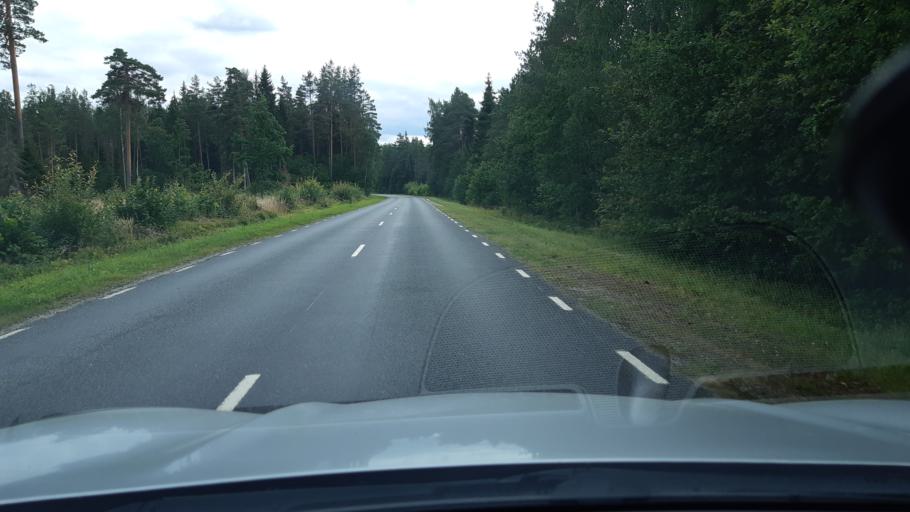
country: EE
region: Raplamaa
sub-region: Maerjamaa vald
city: Marjamaa
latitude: 59.0295
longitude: 24.5538
